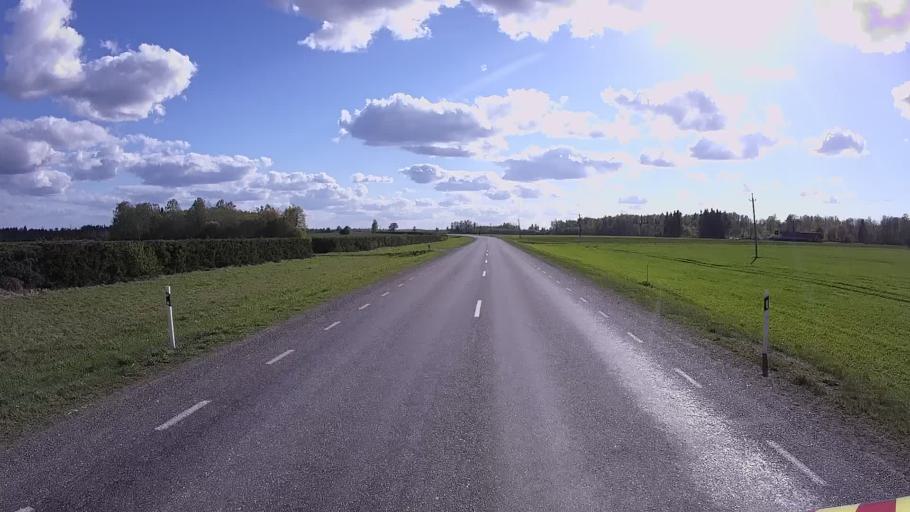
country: EE
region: Jogevamaa
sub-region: Poltsamaa linn
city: Poltsamaa
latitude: 58.6982
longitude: 26.1412
